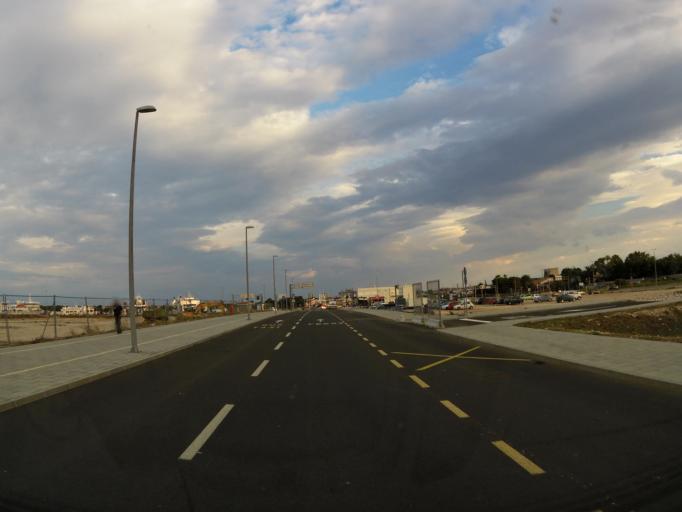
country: HR
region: Zadarska
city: Zadar
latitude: 44.0924
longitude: 15.2608
